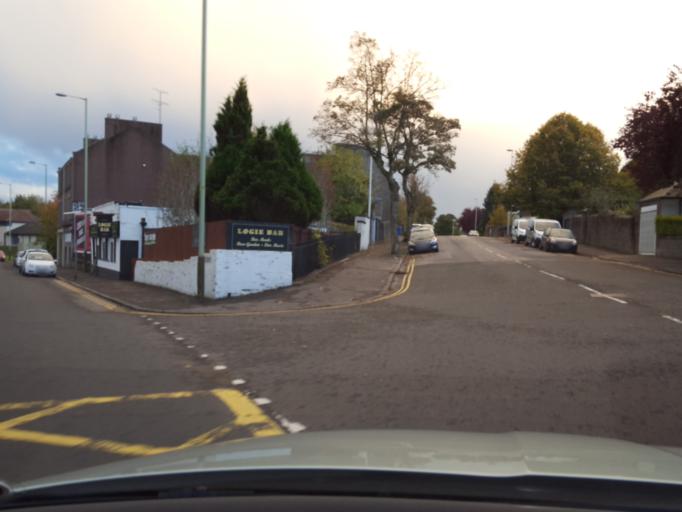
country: GB
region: Scotland
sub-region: Dundee City
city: Dundee
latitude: 56.4683
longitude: -3.0026
